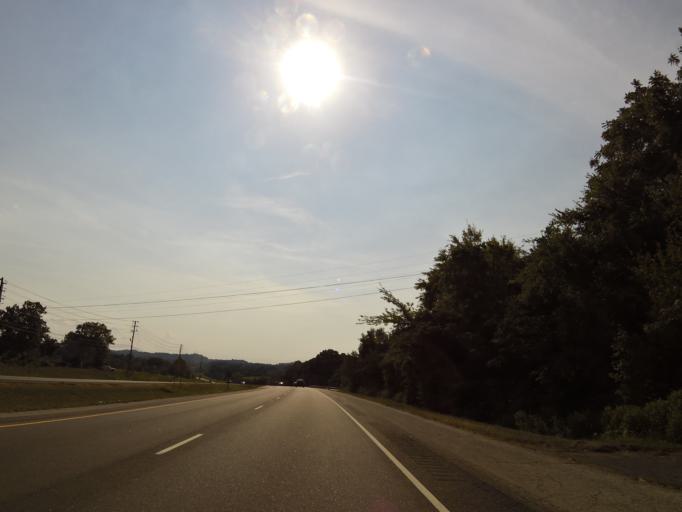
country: US
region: Tennessee
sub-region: Blount County
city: Louisville
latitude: 35.7568
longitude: -84.0866
